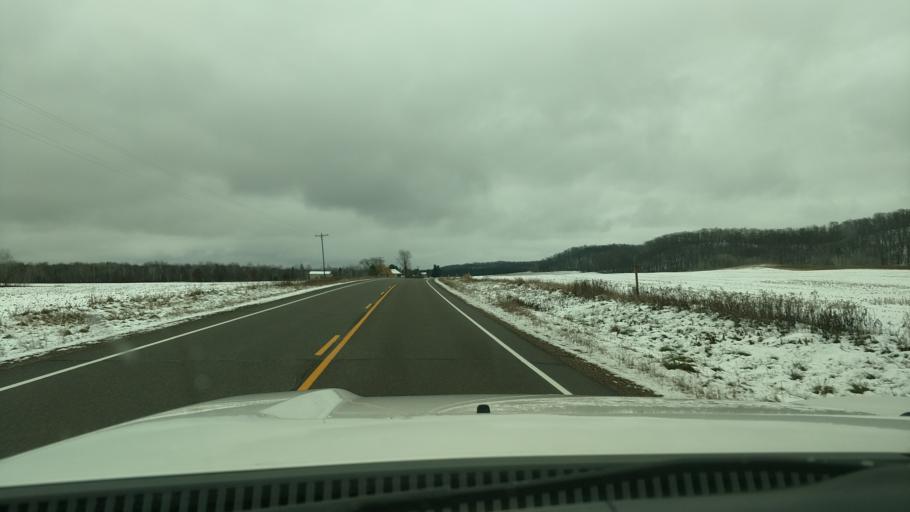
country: US
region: Wisconsin
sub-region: Dunn County
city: Colfax
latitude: 45.1388
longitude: -91.7696
